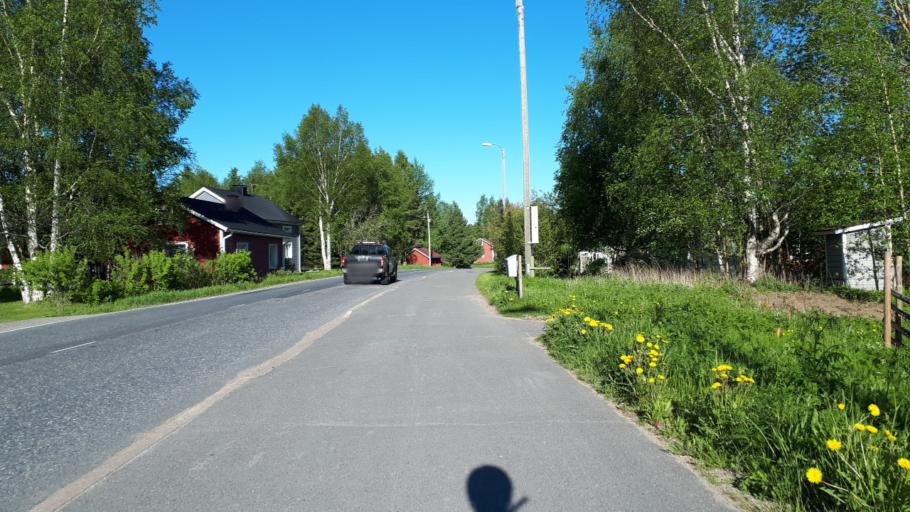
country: FI
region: Northern Ostrobothnia
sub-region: Oulunkaari
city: Ii
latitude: 65.3231
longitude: 25.4504
